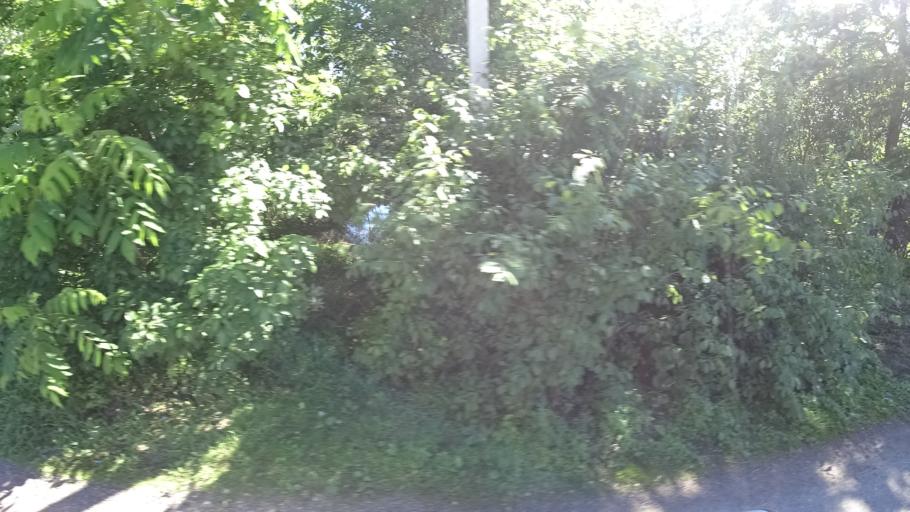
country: RU
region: Khabarovsk Krai
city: Khor
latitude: 47.8860
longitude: 134.9958
